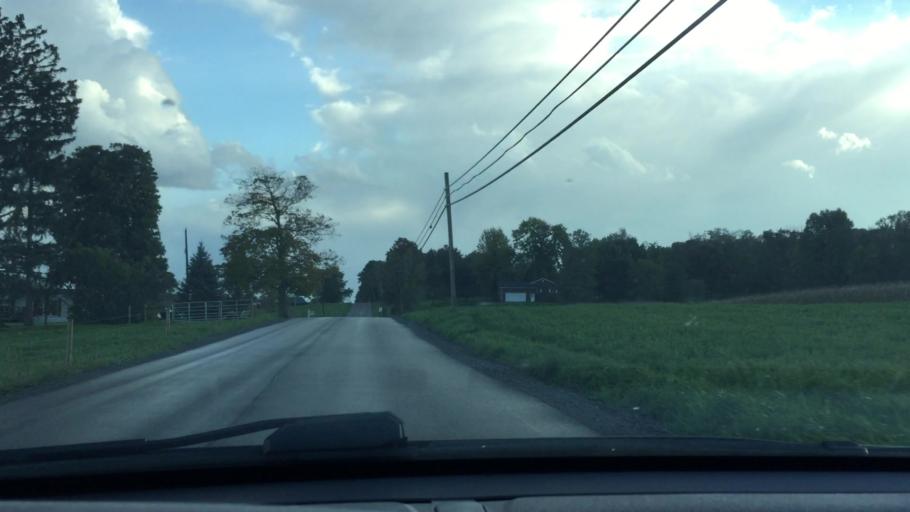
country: US
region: Pennsylvania
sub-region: Lawrence County
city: Bessemer
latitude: 40.9966
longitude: -80.4567
